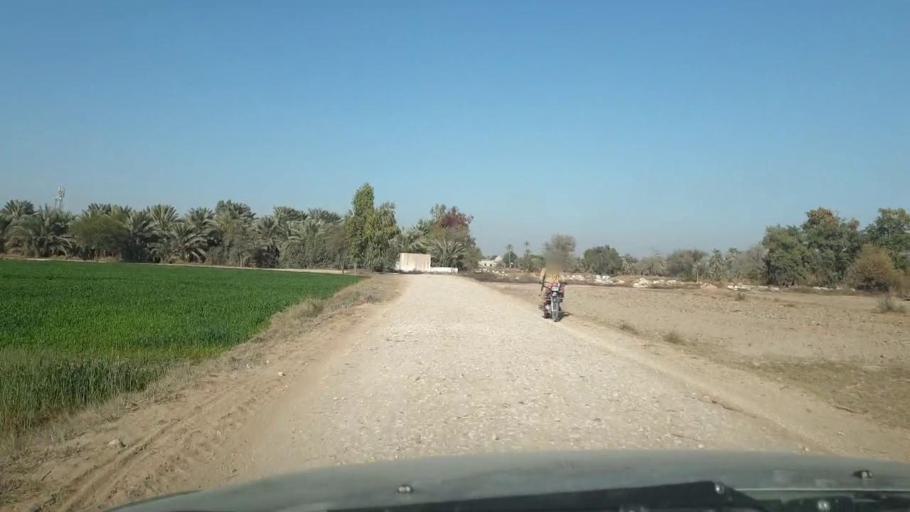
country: PK
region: Sindh
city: Ghotki
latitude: 28.0562
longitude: 69.3393
